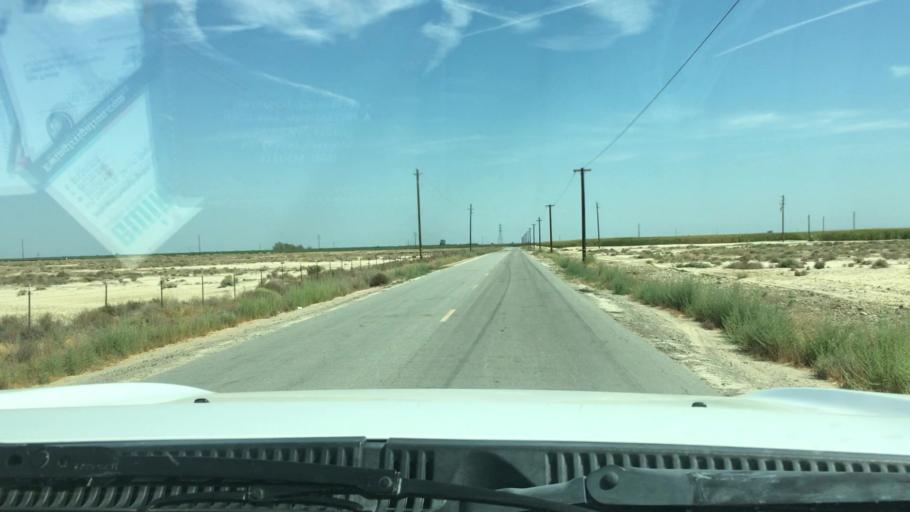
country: US
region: California
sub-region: Kern County
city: Buttonwillow
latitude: 35.4333
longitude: -119.3761
